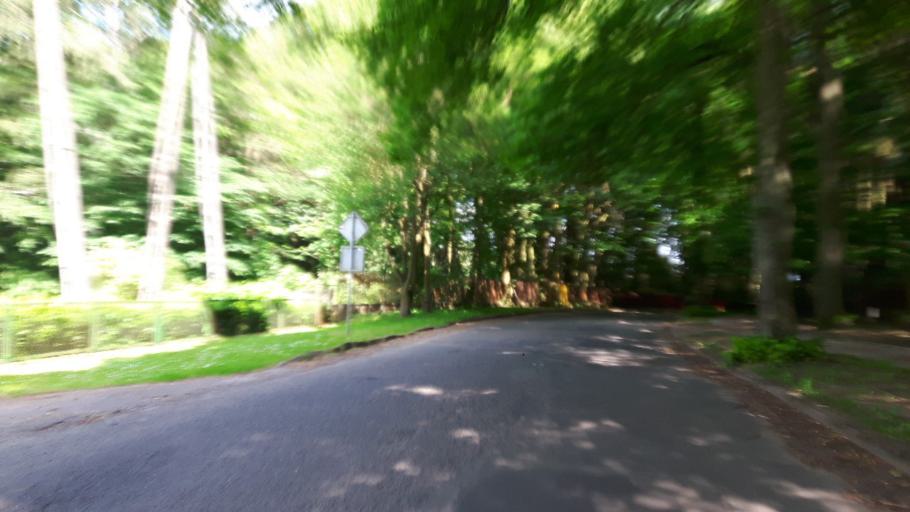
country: PL
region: West Pomeranian Voivodeship
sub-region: Powiat goleniowski
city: Nowogard
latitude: 53.6701
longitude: 15.0939
